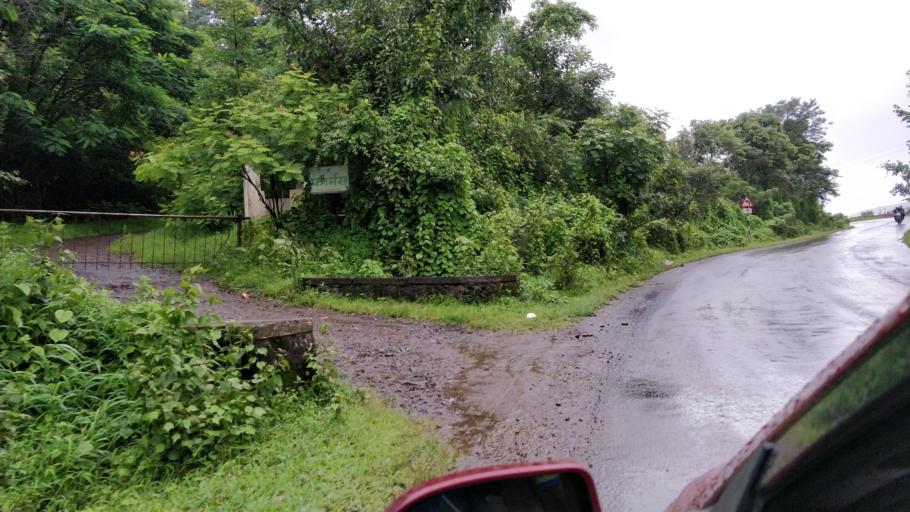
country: IN
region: Maharashtra
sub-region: Pune Division
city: Kharakvasla
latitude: 18.4759
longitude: 73.6547
